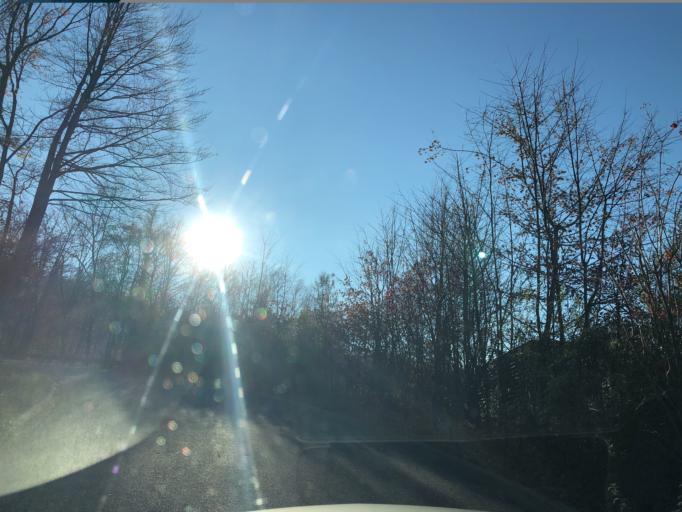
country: DE
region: Hesse
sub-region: Regierungsbezirk Darmstadt
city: Seeheim-Jugenheim
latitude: 49.7597
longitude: 8.6534
